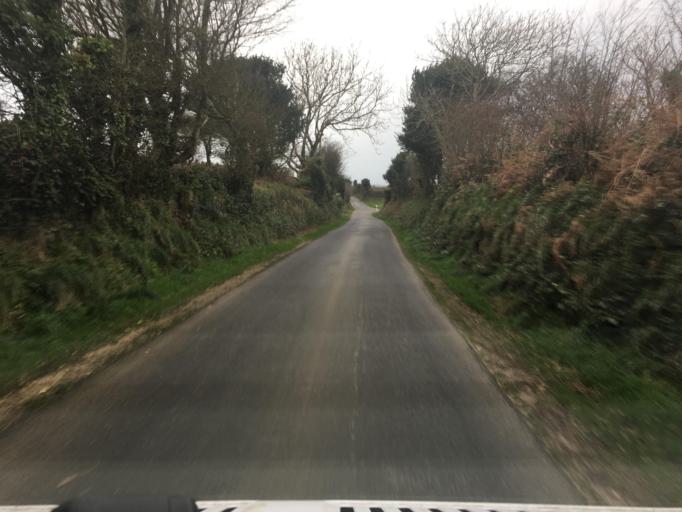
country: FR
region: Lower Normandy
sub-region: Departement de la Manche
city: Beaumont-Hague
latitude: 49.6863
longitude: -1.8719
